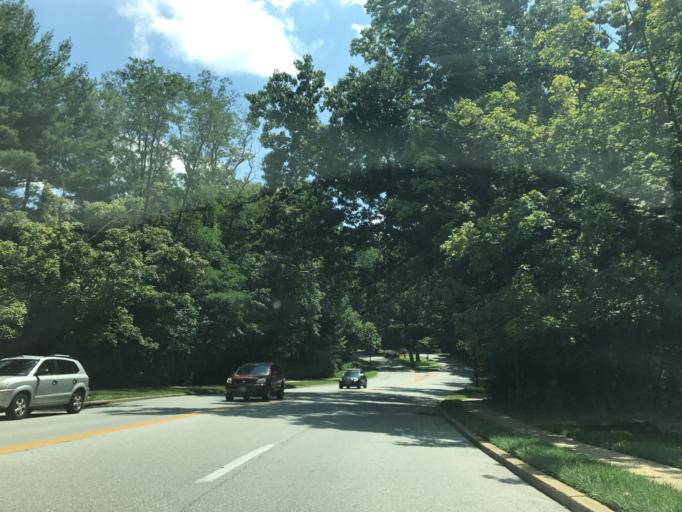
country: US
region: Maryland
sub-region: Howard County
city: Columbia
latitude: 39.2212
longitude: -76.8828
